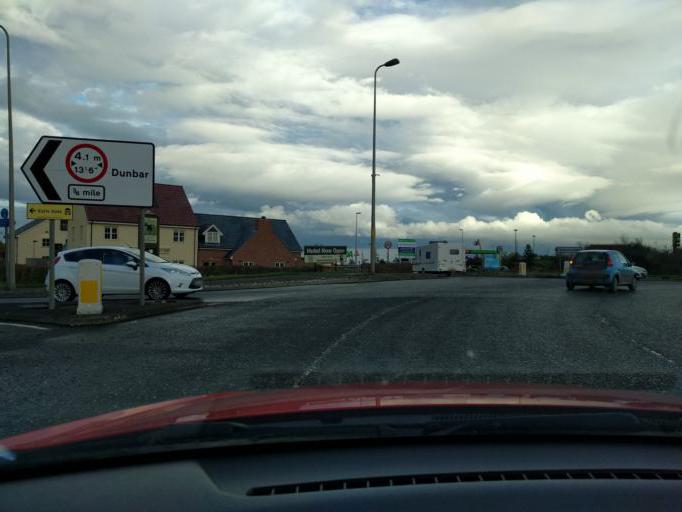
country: GB
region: Scotland
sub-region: East Lothian
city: Dunbar
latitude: 55.9881
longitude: -2.5132
